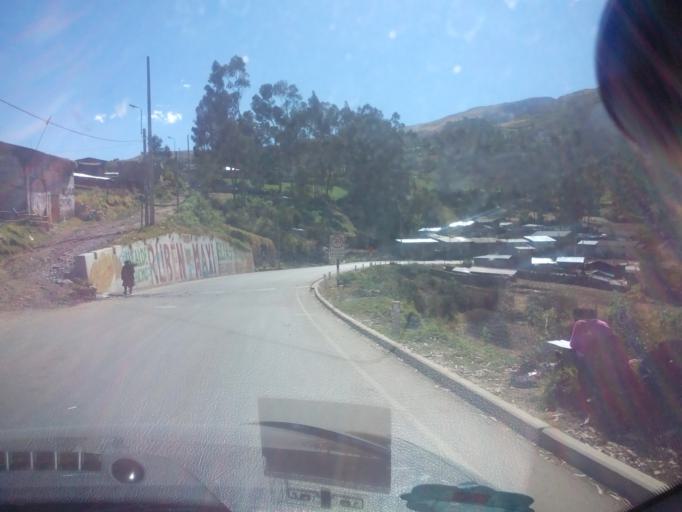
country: PE
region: Apurimac
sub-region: Provincia de Andahuaylas
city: Talavera
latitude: -13.6530
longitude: -73.5275
